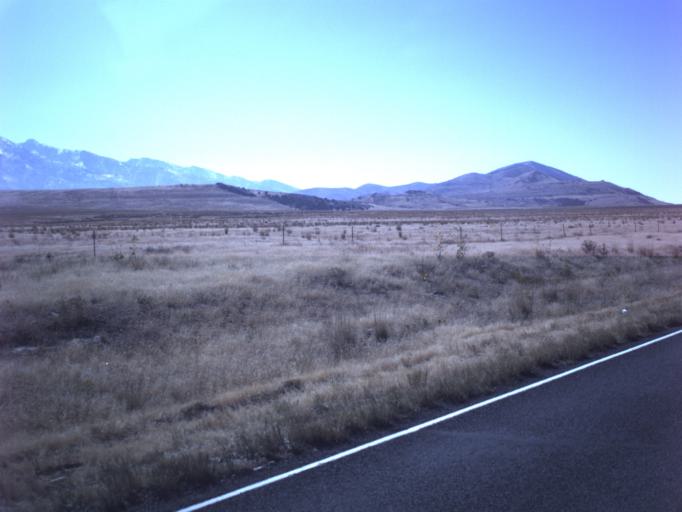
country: US
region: Utah
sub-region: Tooele County
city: Grantsville
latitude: 40.6066
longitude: -112.7090
